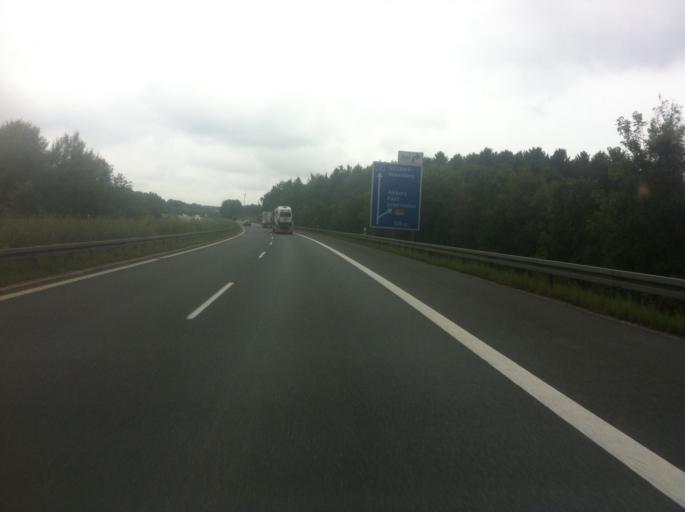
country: DE
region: Bavaria
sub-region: Upper Palatinate
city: Ursensollen
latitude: 49.4073
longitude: 11.7764
